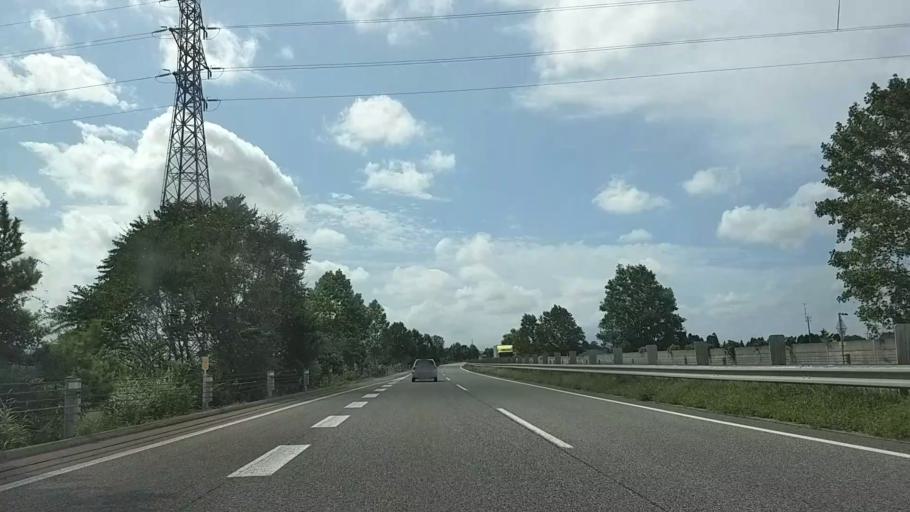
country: JP
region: Toyama
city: Takaoka
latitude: 36.6679
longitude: 137.0292
